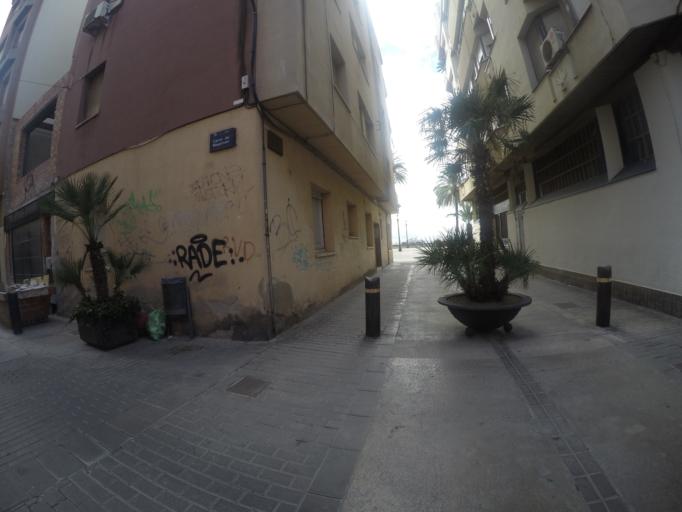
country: ES
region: Catalonia
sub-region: Provincia de Barcelona
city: Badalona
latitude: 41.4495
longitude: 2.2516
